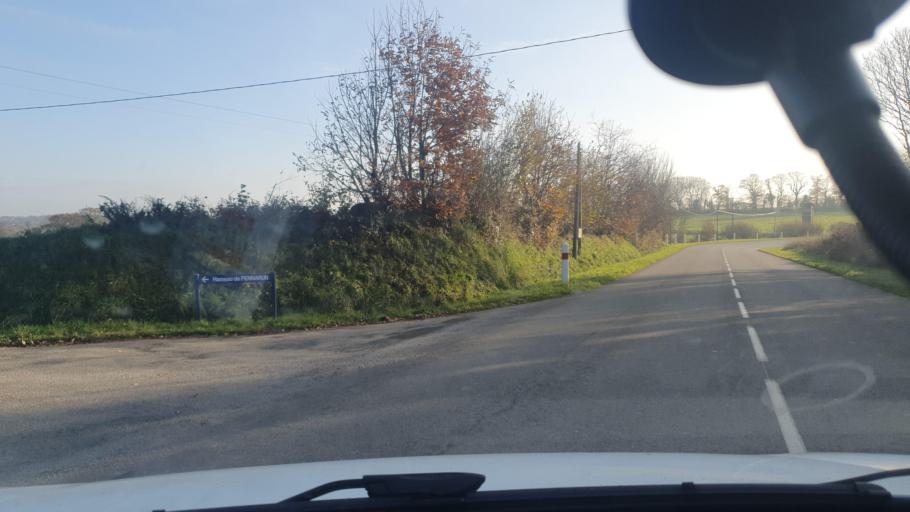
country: FR
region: Brittany
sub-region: Departement du Finistere
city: Briec
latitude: 48.0895
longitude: -4.0036
